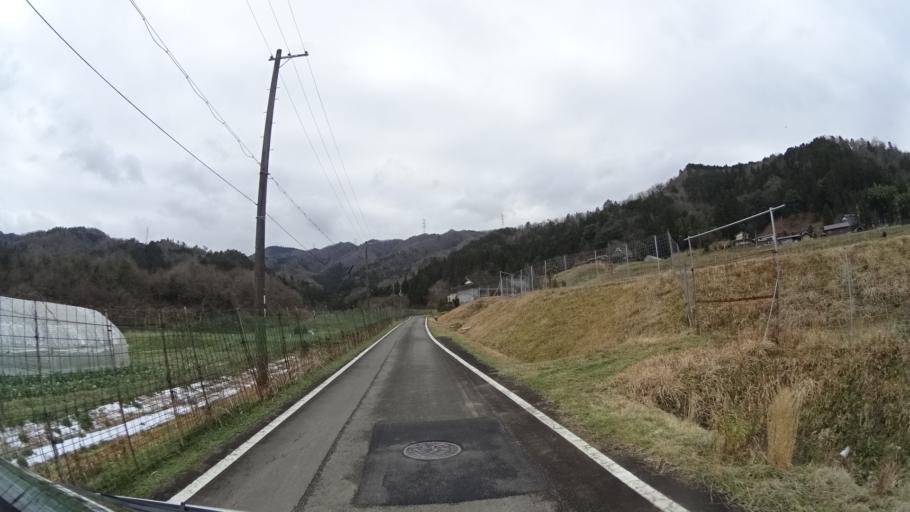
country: JP
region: Kyoto
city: Ayabe
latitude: 35.3229
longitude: 135.3594
